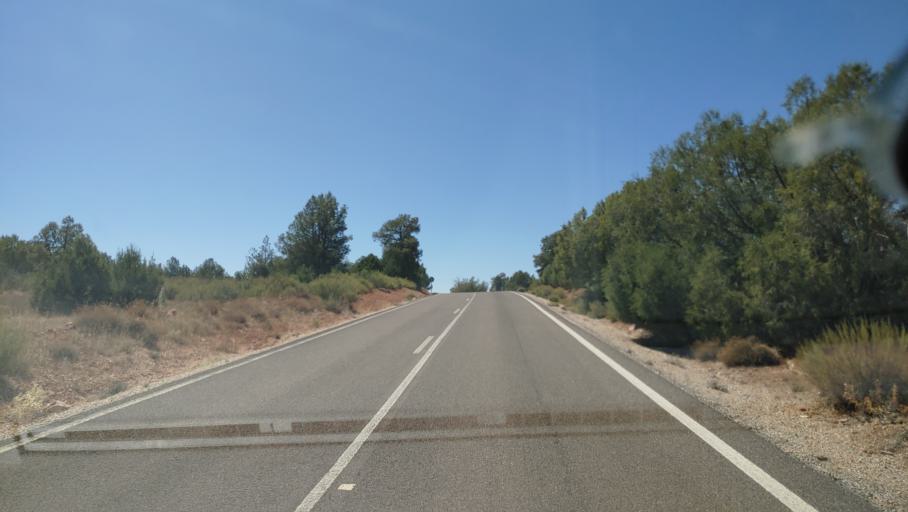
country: ES
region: Castille-La Mancha
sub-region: Provincia de Albacete
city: Ossa de Montiel
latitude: 38.8692
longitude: -2.7919
